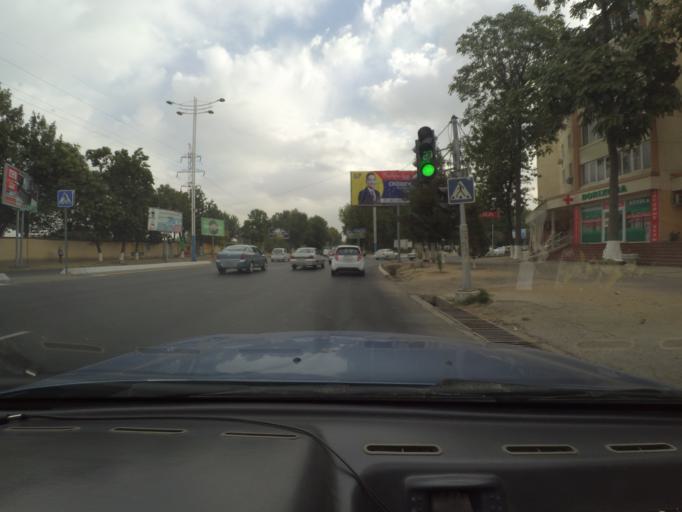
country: UZ
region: Toshkent
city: Salor
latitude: 41.3549
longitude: 69.3568
